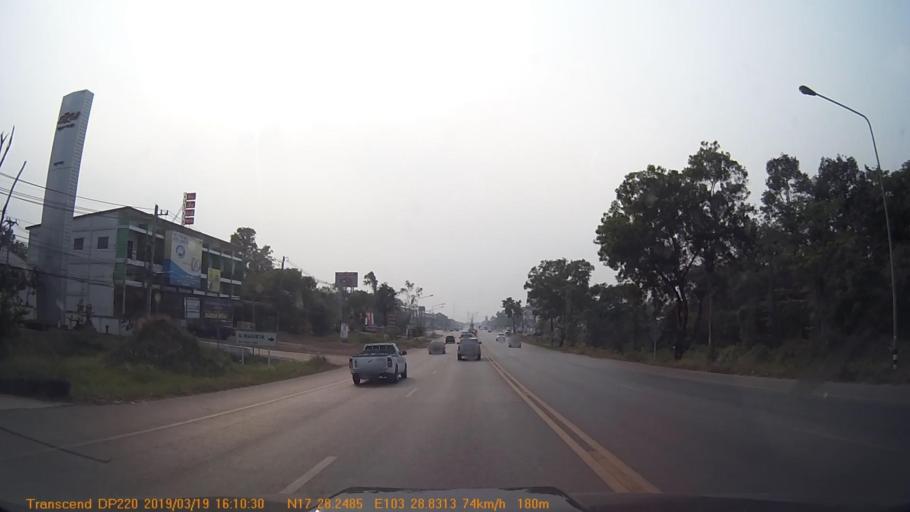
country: TH
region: Sakon Nakhon
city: Sawang Daen Din
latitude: 17.4709
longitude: 103.4801
